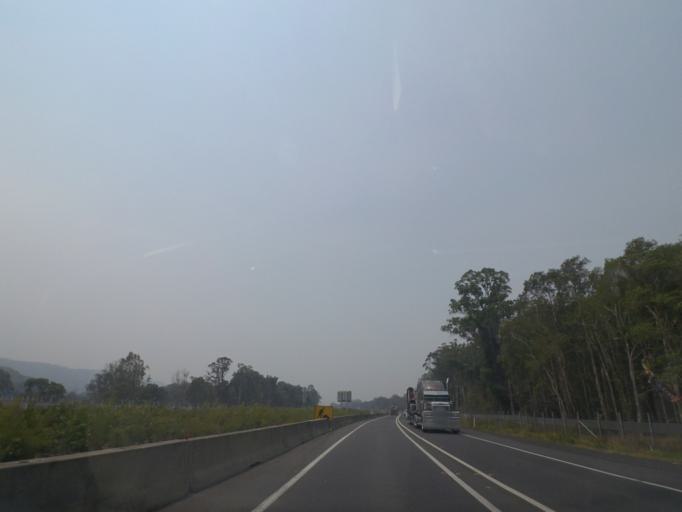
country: AU
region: New South Wales
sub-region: Ballina
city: Ballina
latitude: -28.9162
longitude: 153.4774
